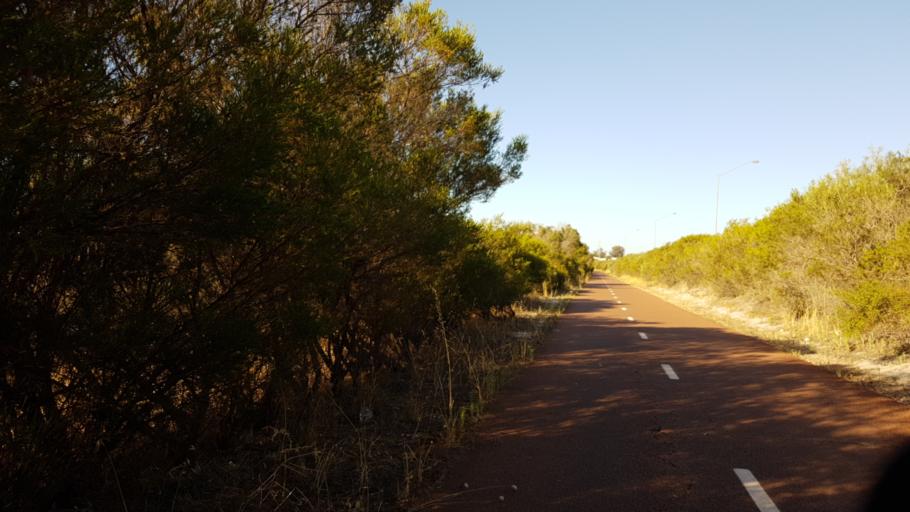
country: AU
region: Western Australia
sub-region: Kwinana
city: Wellard
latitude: -32.2668
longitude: 115.8491
